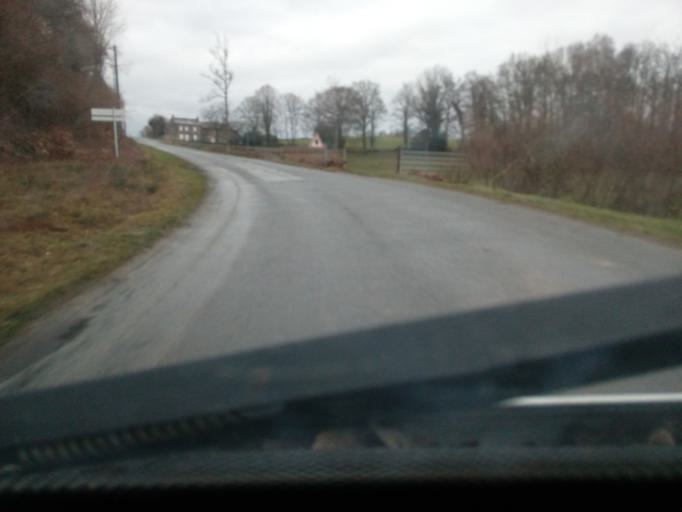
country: FR
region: Limousin
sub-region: Departement de la Creuse
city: Felletin
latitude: 45.8604
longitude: 2.2189
